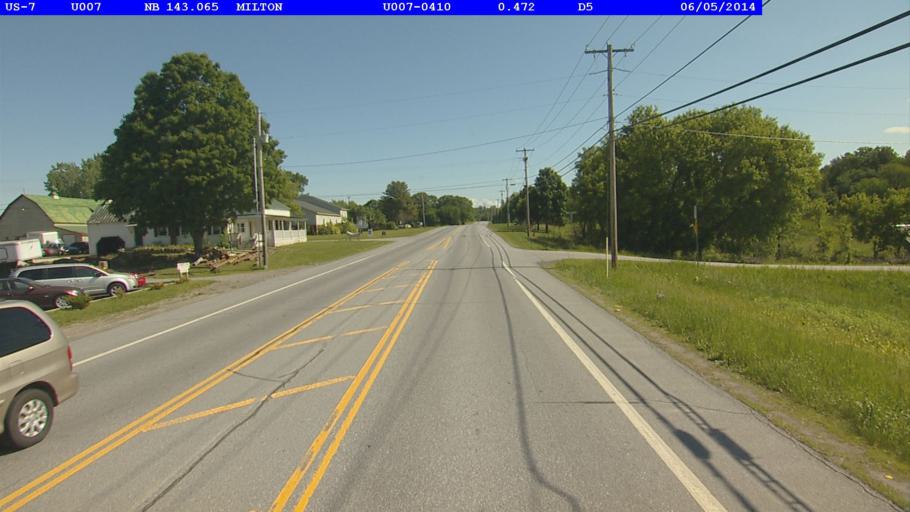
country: US
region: Vermont
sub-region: Chittenden County
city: Colchester
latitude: 44.6020
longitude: -73.1613
